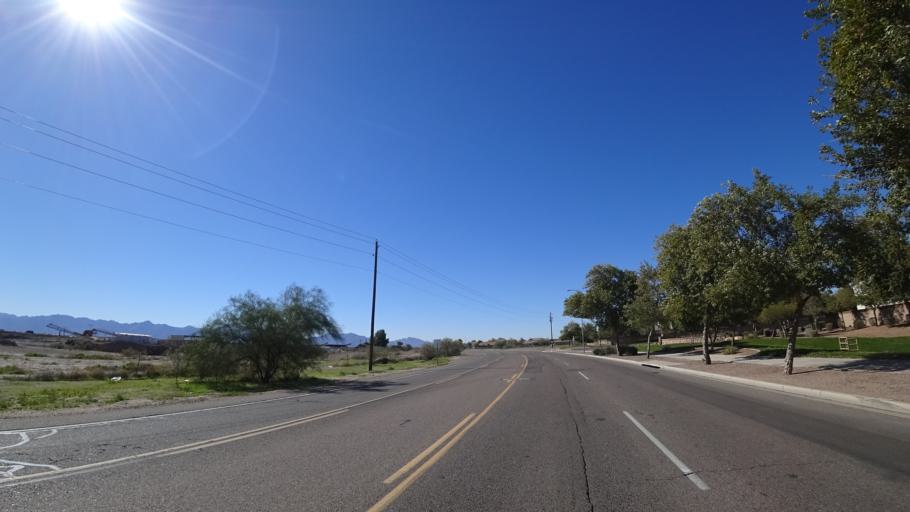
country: US
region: Arizona
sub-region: Maricopa County
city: Laveen
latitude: 33.4116
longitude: -112.1725
